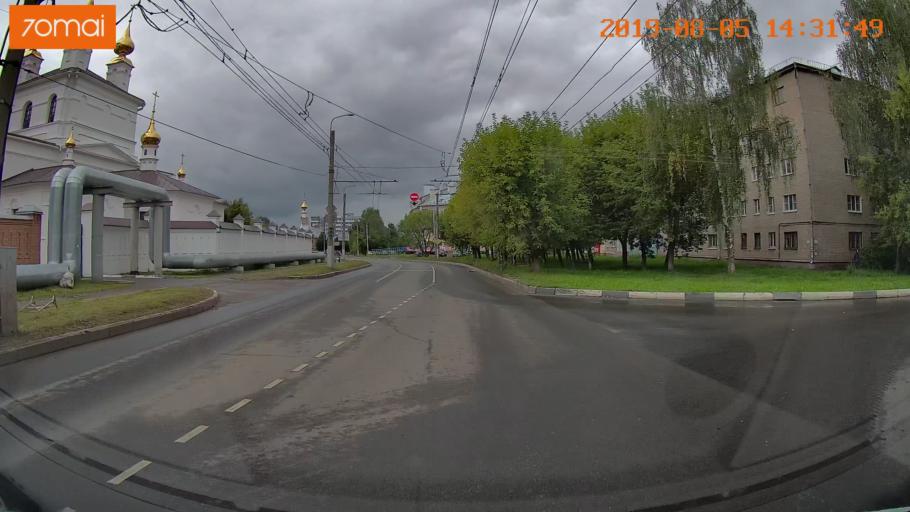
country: RU
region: Ivanovo
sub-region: Gorod Ivanovo
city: Ivanovo
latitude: 56.9887
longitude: 40.9970
